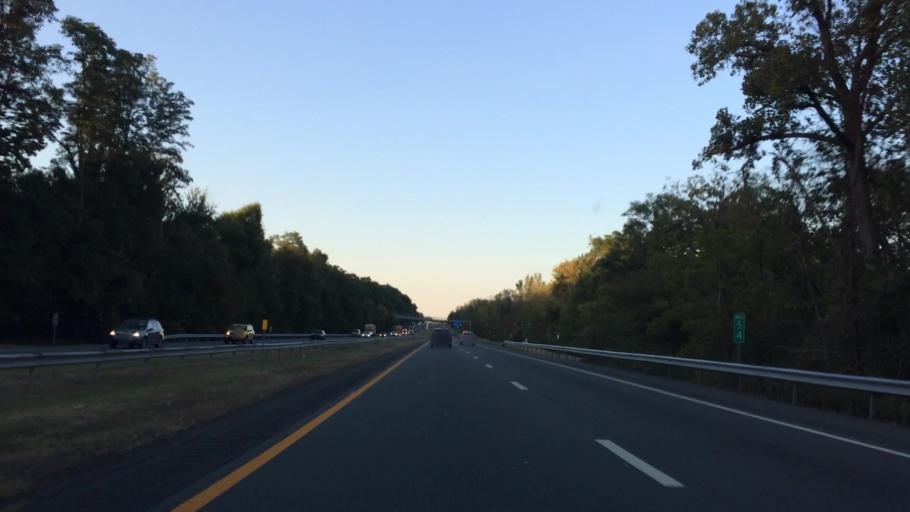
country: US
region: New York
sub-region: Orange County
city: Firthcliffe
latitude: 41.4241
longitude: -74.0685
